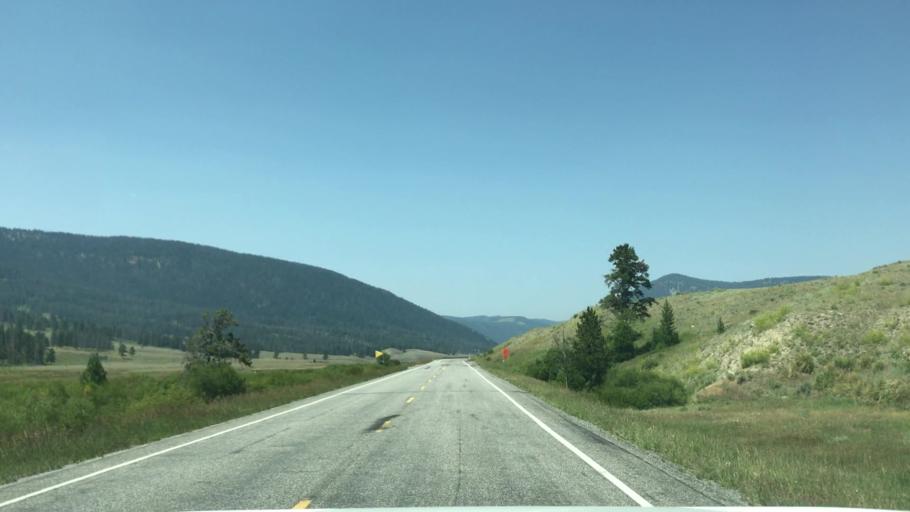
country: US
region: Montana
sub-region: Gallatin County
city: Big Sky
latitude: 45.0414
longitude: -111.1253
